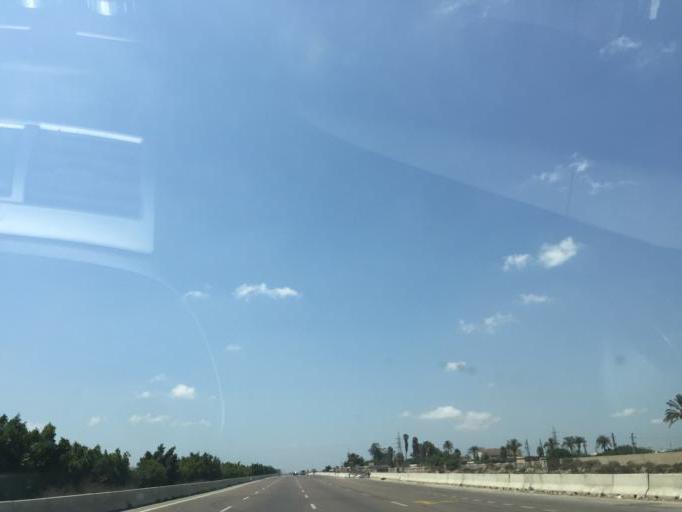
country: EG
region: Alexandria
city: Alexandria
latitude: 30.9549
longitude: 29.8383
